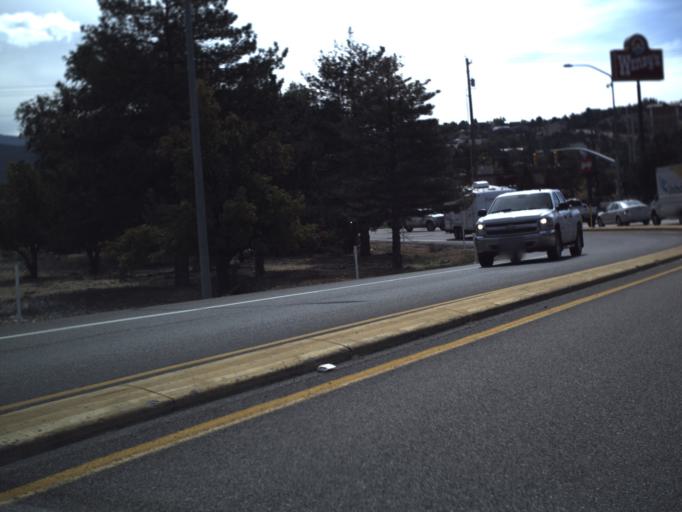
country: US
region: Utah
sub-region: Iron County
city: Cedar City
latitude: 37.6819
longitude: -113.0785
